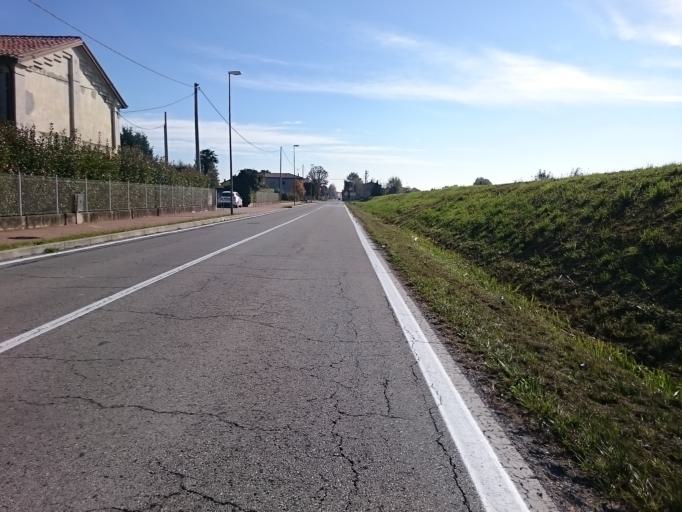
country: IT
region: Veneto
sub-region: Provincia di Padova
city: Piazzola sul Brenta
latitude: 45.5483
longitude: 11.7716
